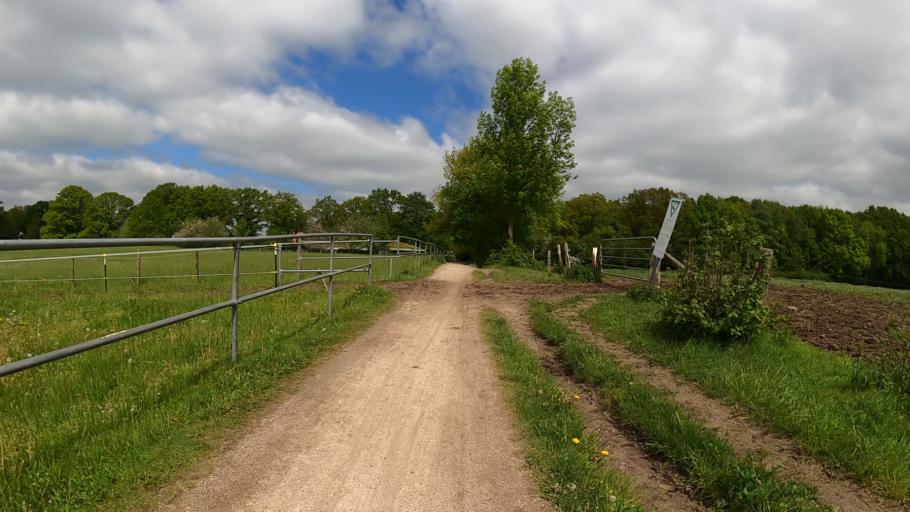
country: DE
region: Hamburg
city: Wohldorf-Ohlstedt
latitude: 53.7131
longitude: 10.1409
